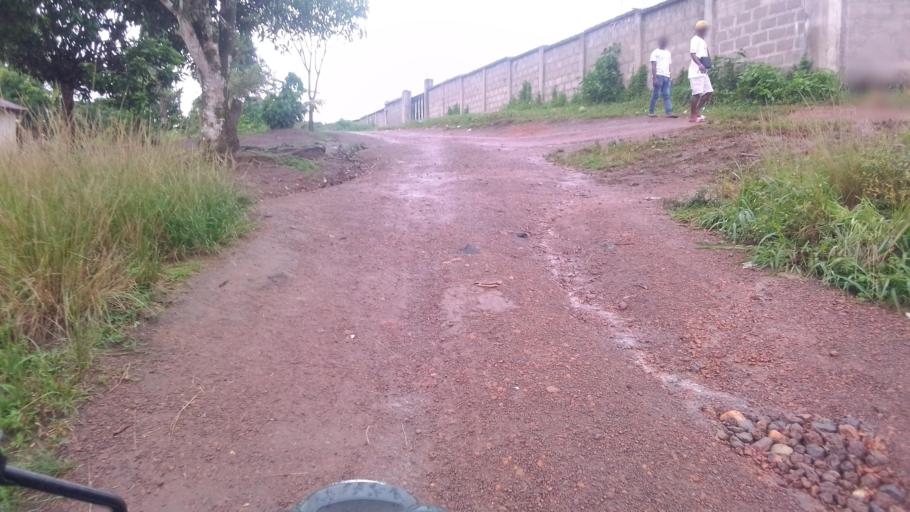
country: SL
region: Eastern Province
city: Kenema
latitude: 7.8503
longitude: -11.1829
